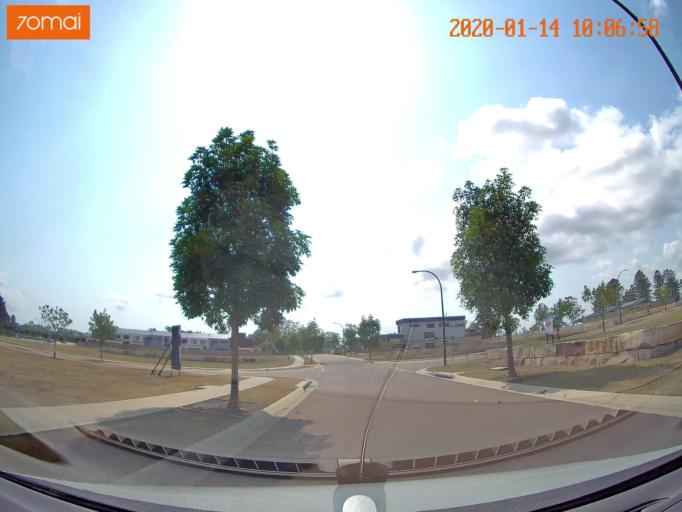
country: AU
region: New South Wales
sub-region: Wyong Shire
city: Kingfisher Shores
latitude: -33.1248
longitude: 151.5386
